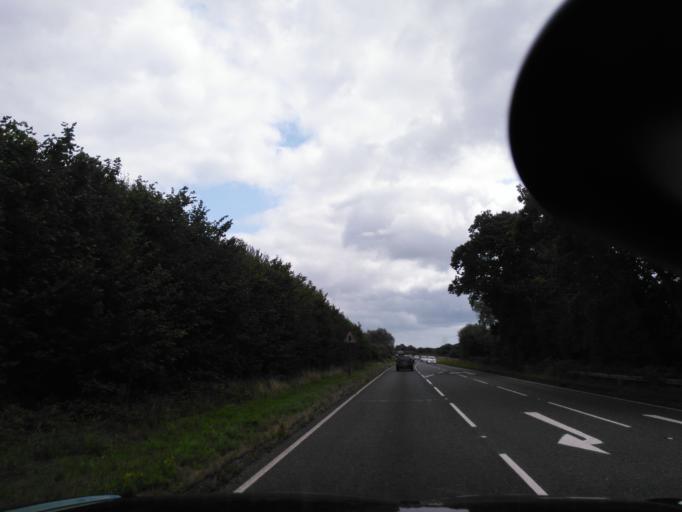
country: GB
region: England
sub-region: Dorset
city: Lytchett Matravers
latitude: 50.7342
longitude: -2.0751
